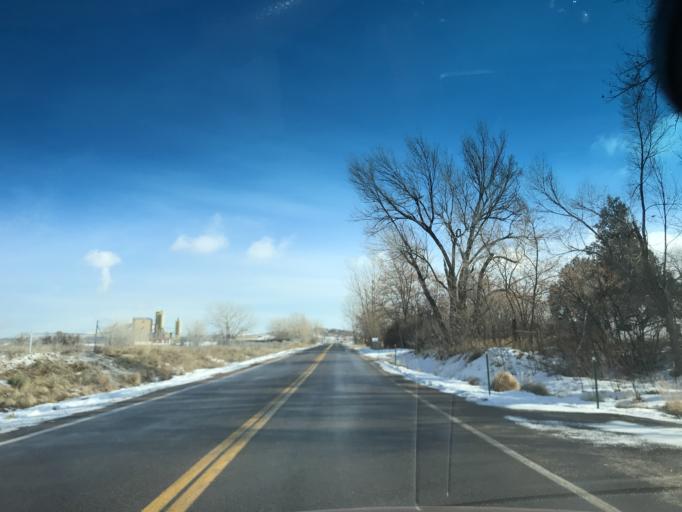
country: US
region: Colorado
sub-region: Douglas County
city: Highlands Ranch
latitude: 39.4710
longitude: -104.9971
